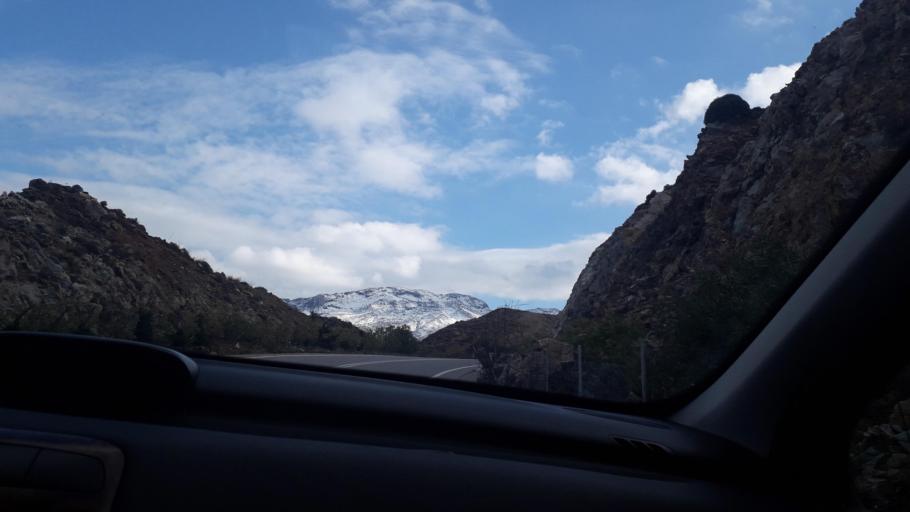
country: GR
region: Crete
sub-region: Nomos Rethymnis
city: Agia Foteini
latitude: 35.2658
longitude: 24.5641
